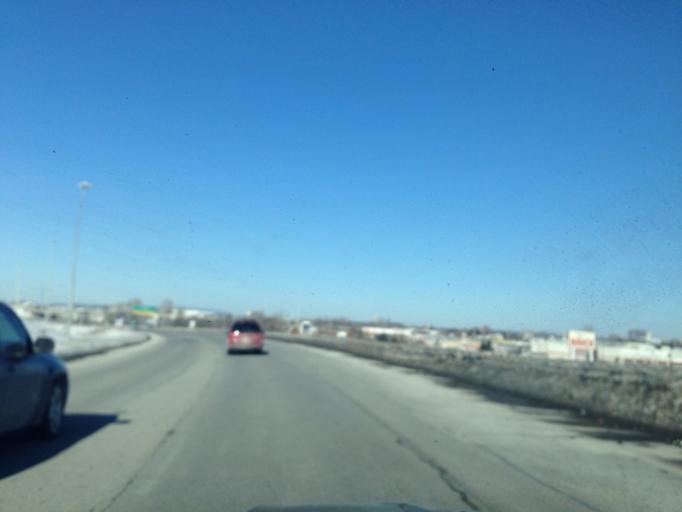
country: CA
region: Ontario
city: Ottawa
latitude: 45.4120
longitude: -75.6015
